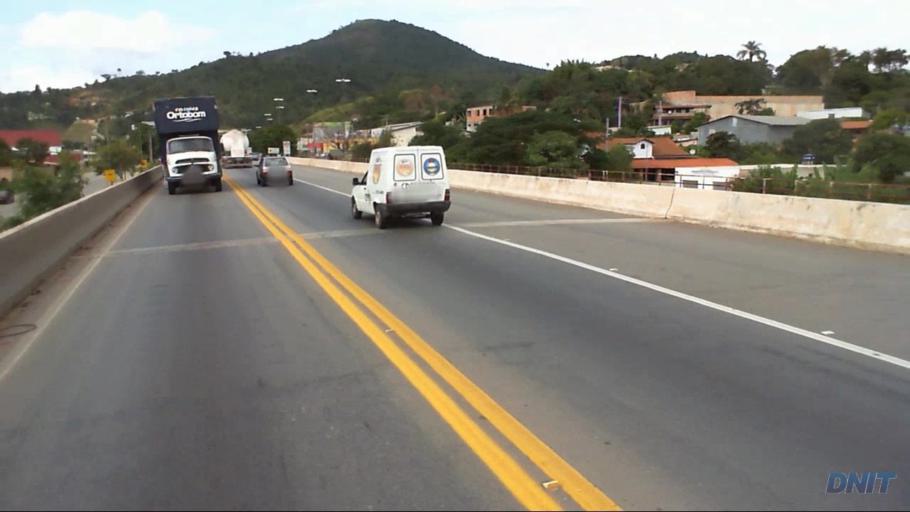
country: BR
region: Minas Gerais
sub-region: Santa Luzia
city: Santa Luzia
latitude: -19.8416
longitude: -43.8679
